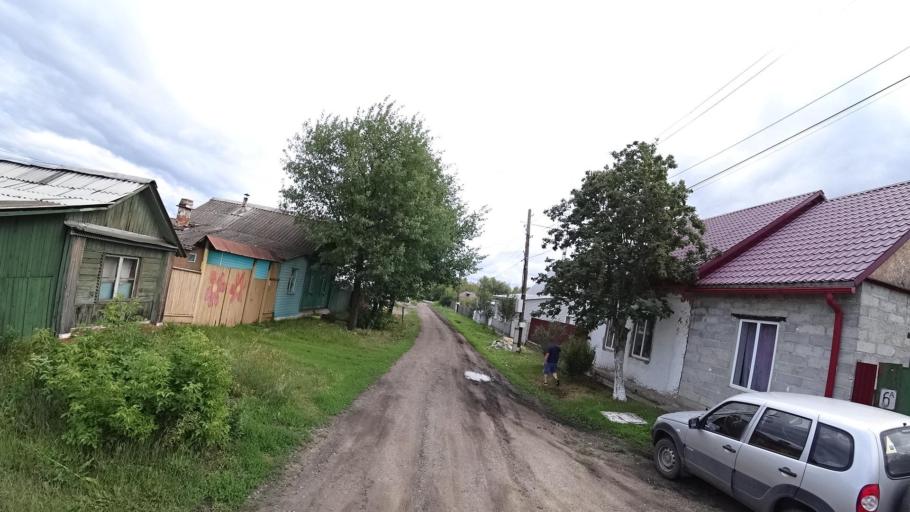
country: RU
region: Sverdlovsk
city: Kamyshlov
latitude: 56.8549
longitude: 62.6979
